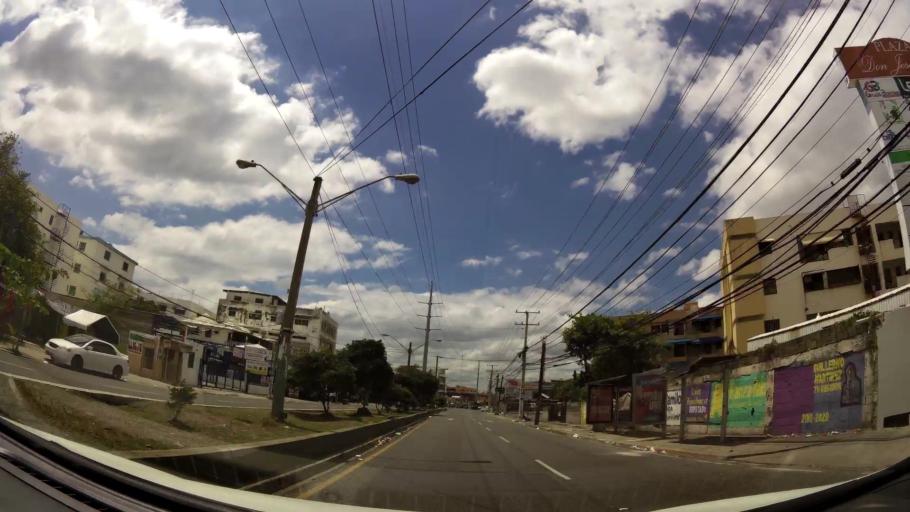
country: DO
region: Nacional
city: Bella Vista
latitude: 18.4340
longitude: -69.9610
